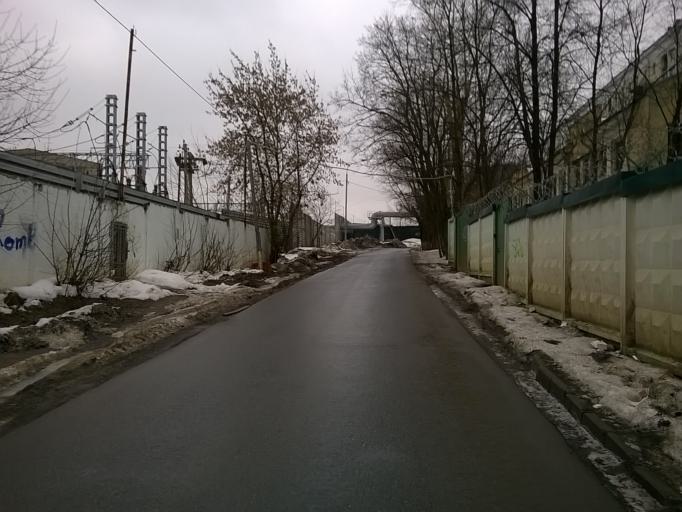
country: RU
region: Moscow
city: Lefortovo
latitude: 55.7774
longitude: 37.7112
